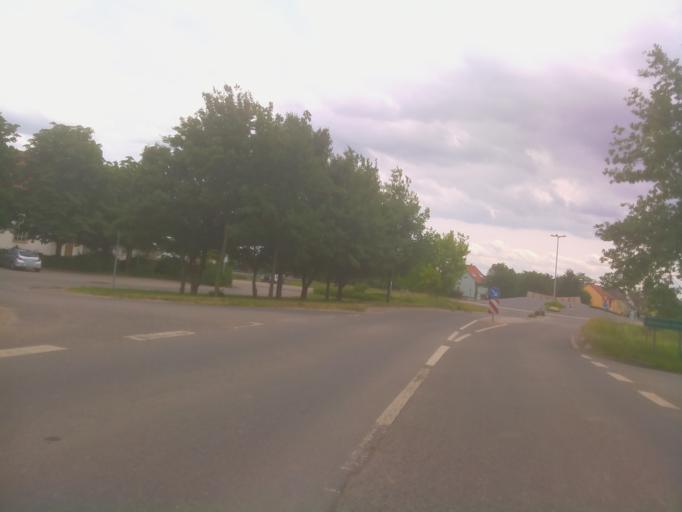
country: DE
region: Rheinland-Pfalz
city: Lambsheim
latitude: 49.5203
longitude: 8.2868
